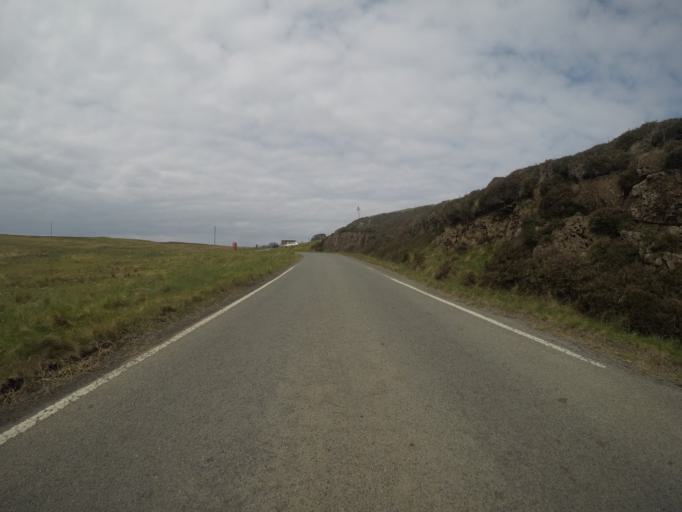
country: GB
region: Scotland
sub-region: Highland
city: Portree
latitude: 57.6837
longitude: -6.3260
